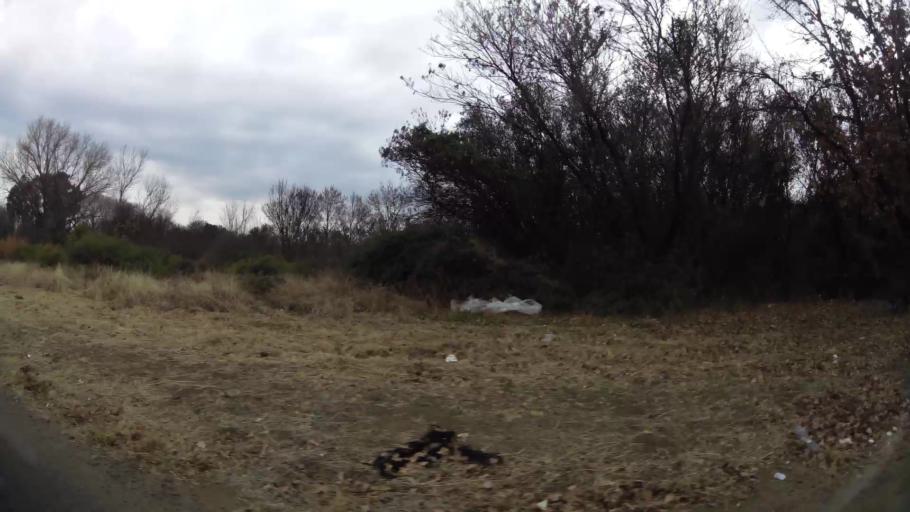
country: ZA
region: Orange Free State
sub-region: Fezile Dabi District Municipality
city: Kroonstad
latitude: -27.6507
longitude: 27.2439
